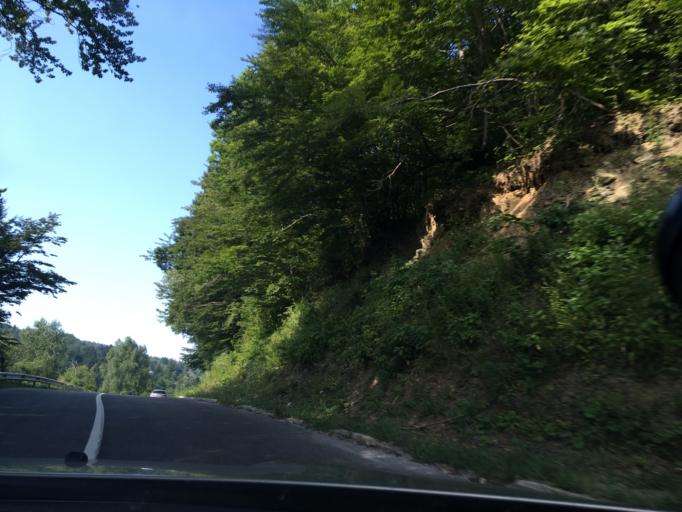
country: HR
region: Primorsko-Goranska
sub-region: Grad Delnice
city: Delnice
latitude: 45.4242
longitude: 14.8289
